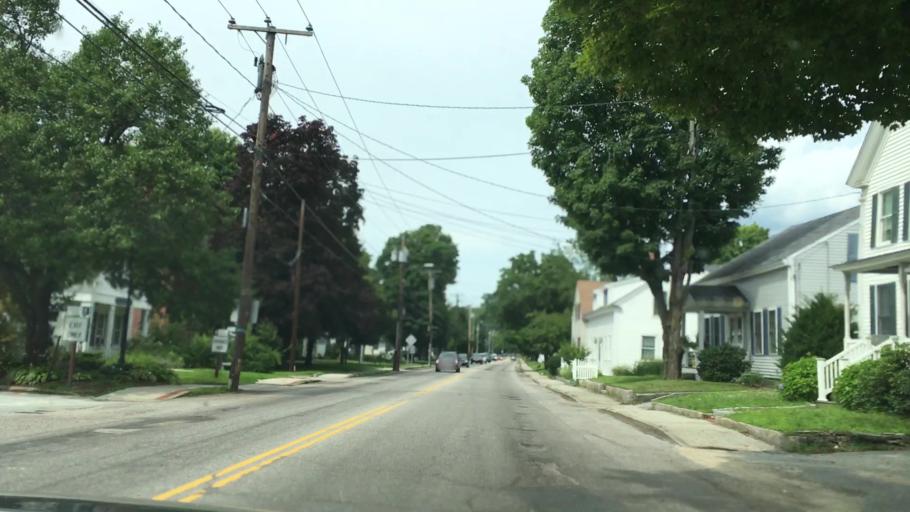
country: US
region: New Hampshire
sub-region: Hillsborough County
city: Peterborough
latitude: 42.8779
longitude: -71.9478
